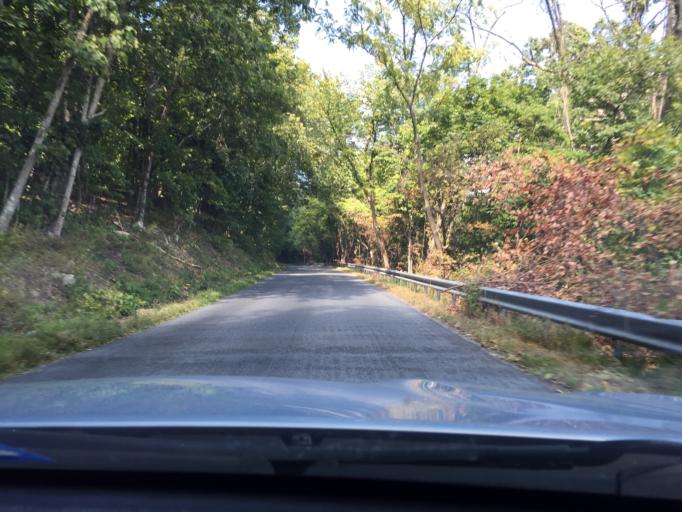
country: US
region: Virginia
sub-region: Page County
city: Luray
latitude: 38.7147
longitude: -78.5150
